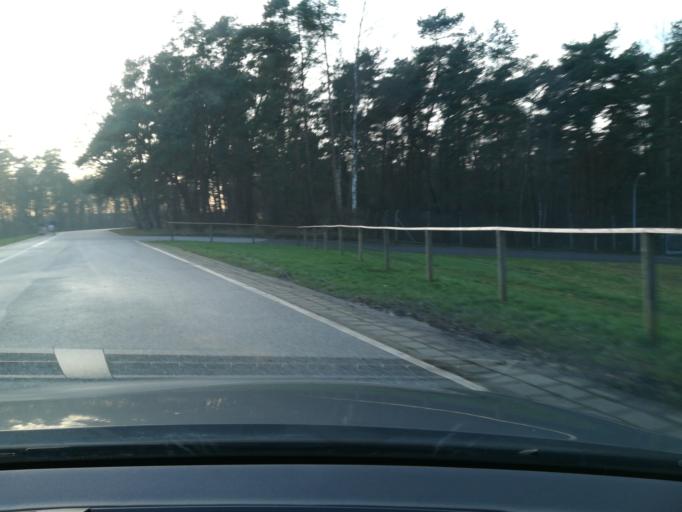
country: DE
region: Schleswig-Holstein
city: Escheburg
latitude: 53.4448
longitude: 10.3162
